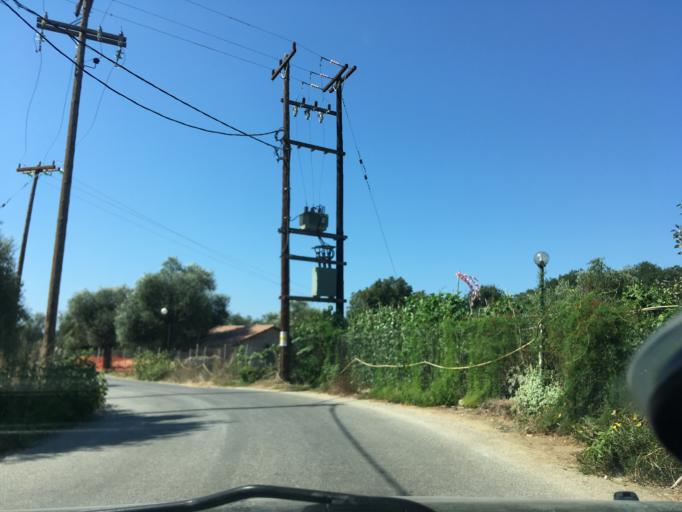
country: GR
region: Ionian Islands
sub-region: Nomos Kerkyras
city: Perivoli
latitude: 39.4216
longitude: 19.9894
